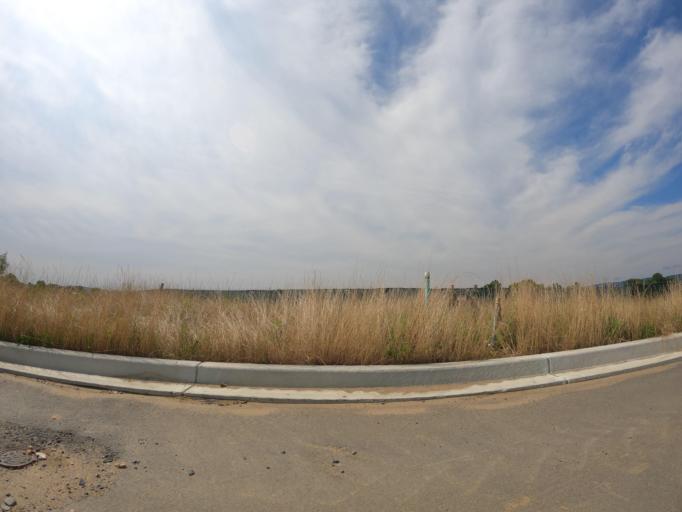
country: US
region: Maryland
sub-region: Frederick County
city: Brunswick
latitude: 39.3205
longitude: -77.6300
